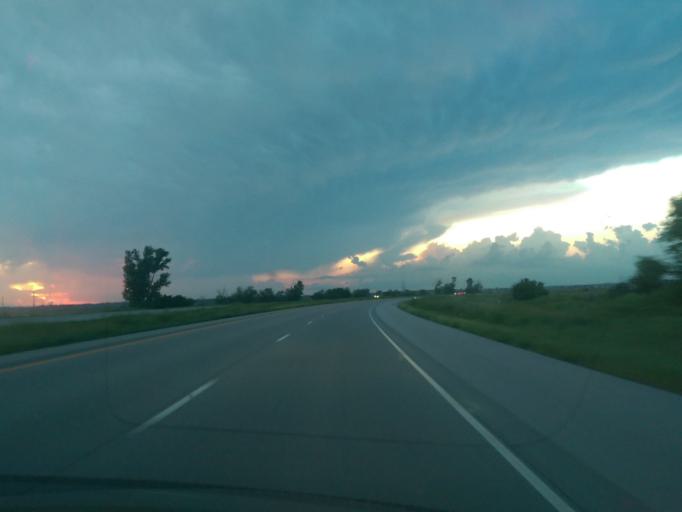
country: US
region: Nebraska
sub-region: Otoe County
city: Nebraska City
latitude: 40.7246
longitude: -95.8140
